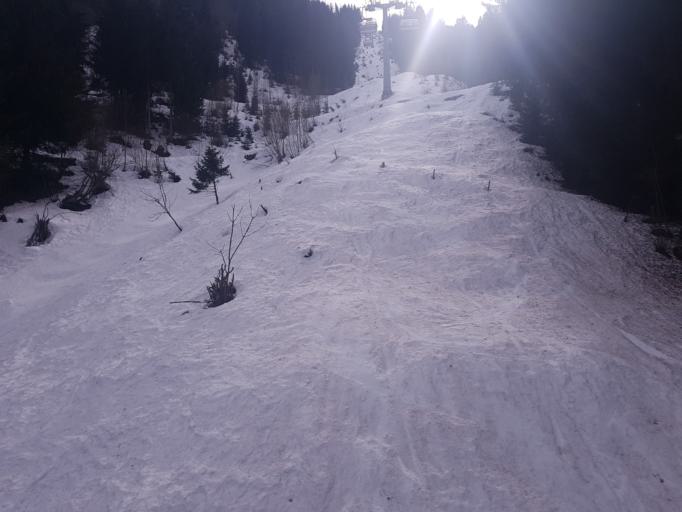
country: AT
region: Tyrol
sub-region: Politischer Bezirk Kufstein
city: Worgl
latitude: 47.4436
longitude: 12.0865
